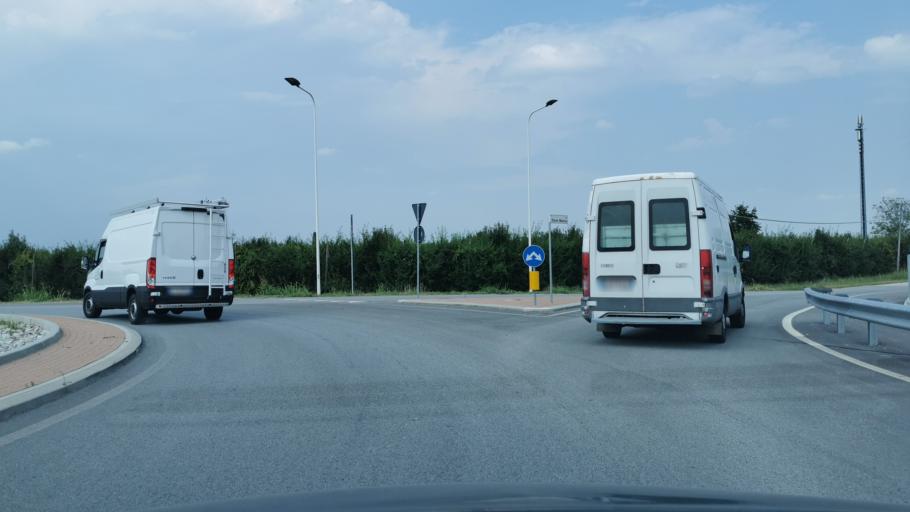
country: IT
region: Piedmont
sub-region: Provincia di Cuneo
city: Roata Rossi
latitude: 44.4610
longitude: 7.5392
